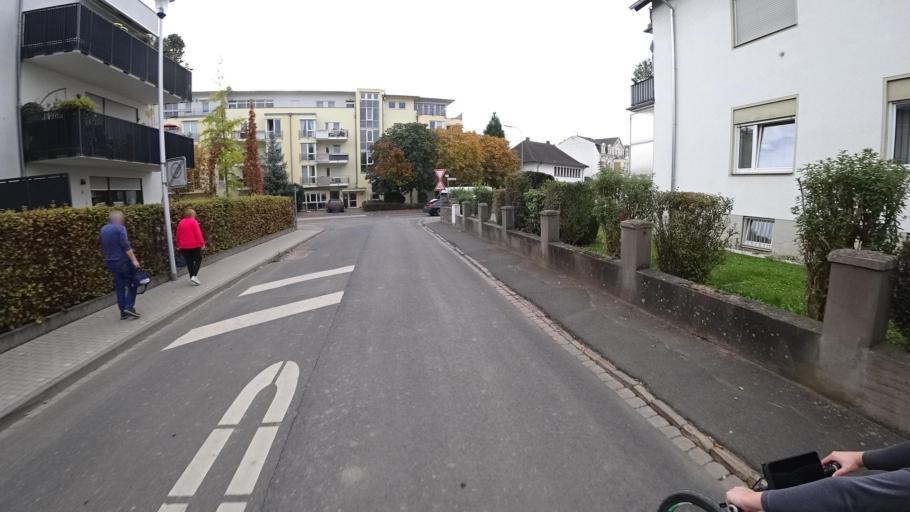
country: DE
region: Rheinland-Pfalz
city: Bad Neuenahr-Ahrweiler
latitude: 50.5463
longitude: 7.1321
